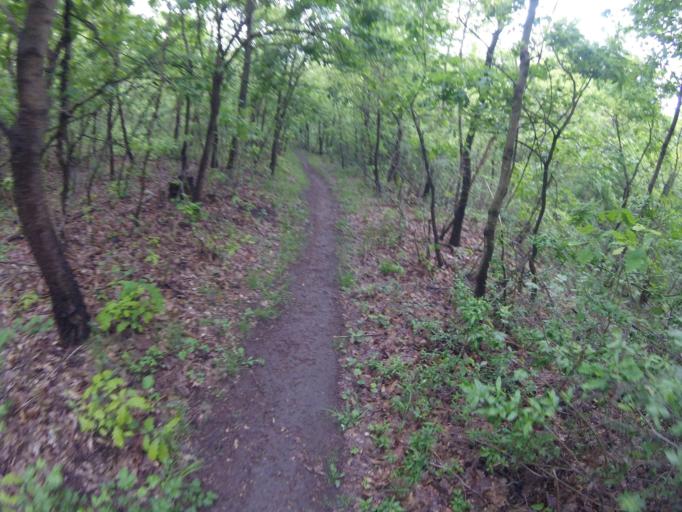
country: HU
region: Nograd
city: Matraverebely
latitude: 47.9845
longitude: 19.7611
